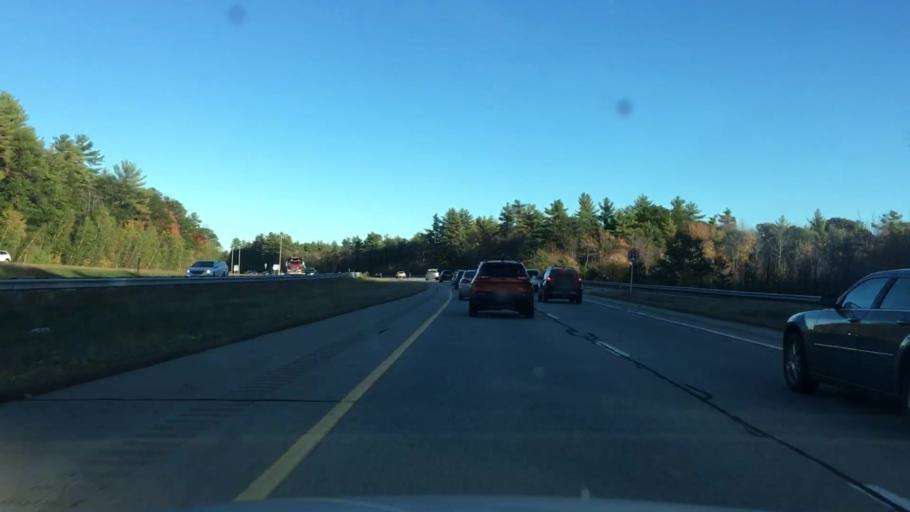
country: US
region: New Hampshire
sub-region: Rockingham County
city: Epping
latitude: 43.0260
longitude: -71.1141
